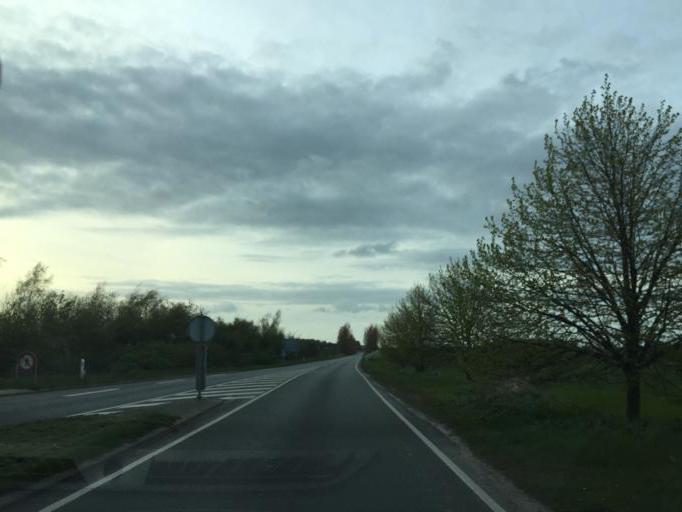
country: DK
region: South Denmark
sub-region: Faaborg-Midtfyn Kommune
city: Ringe
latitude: 55.1821
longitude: 10.5306
